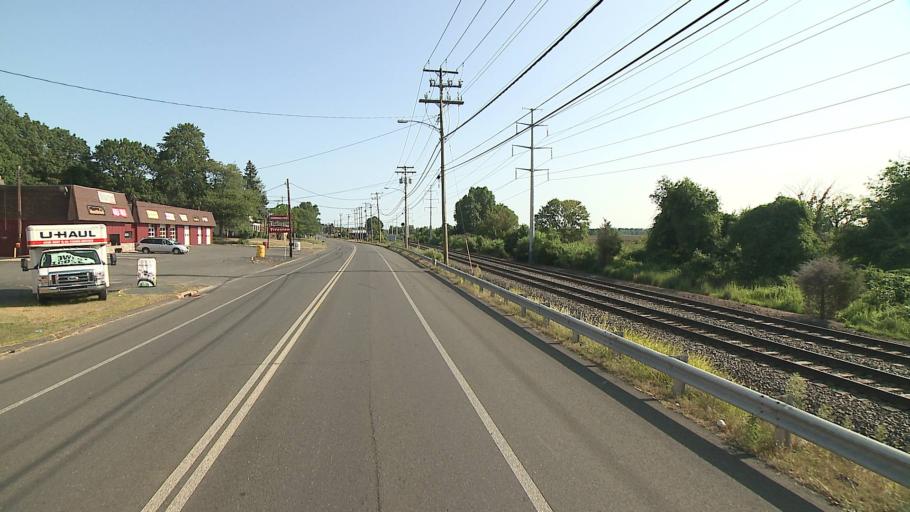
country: US
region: Connecticut
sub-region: New Haven County
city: Hamden
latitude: 41.3485
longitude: -72.8931
